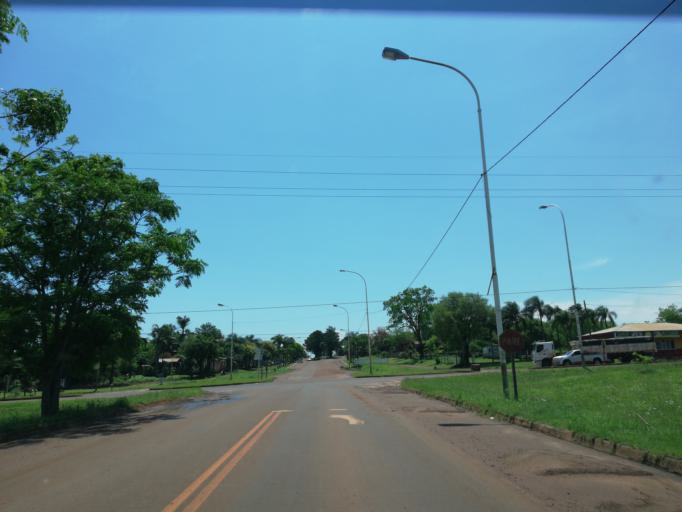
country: AR
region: Misiones
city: Santa Ana
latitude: -27.3773
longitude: -55.5757
